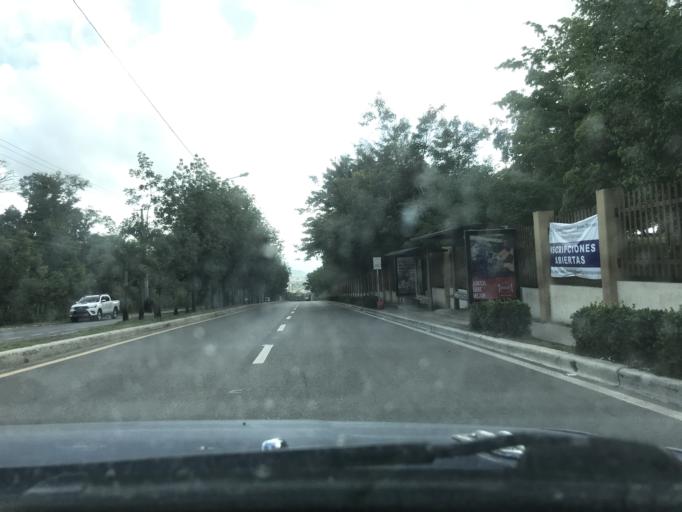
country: DO
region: Santiago
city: Santiago de los Caballeros
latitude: 19.4263
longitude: -70.7298
